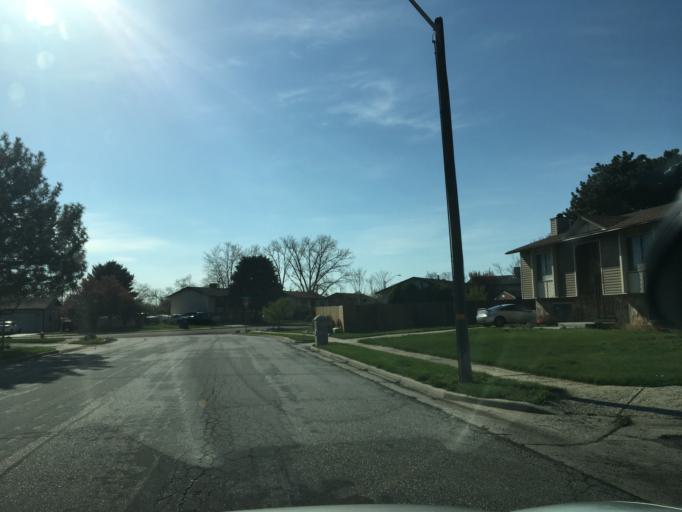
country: US
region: Utah
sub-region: Davis County
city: Layton
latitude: 41.0754
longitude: -111.9898
